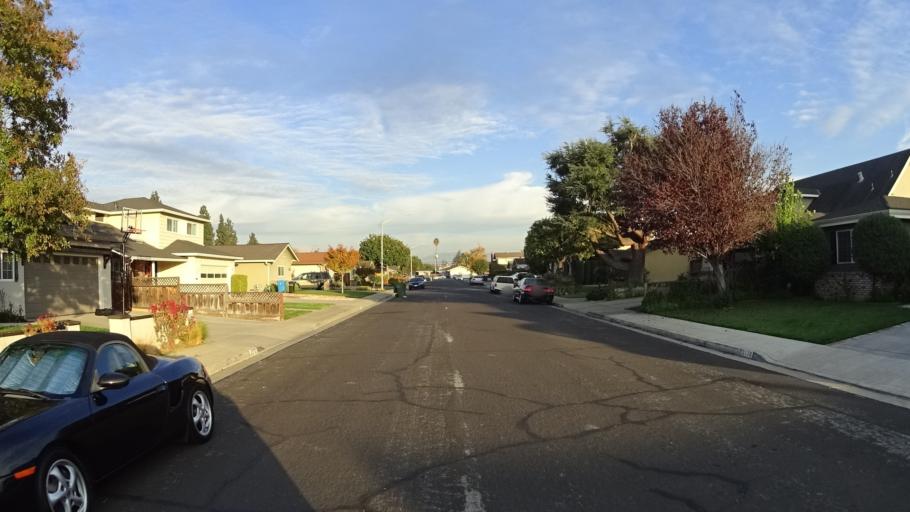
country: US
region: California
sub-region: Santa Clara County
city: Santa Clara
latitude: 37.3485
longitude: -121.9624
